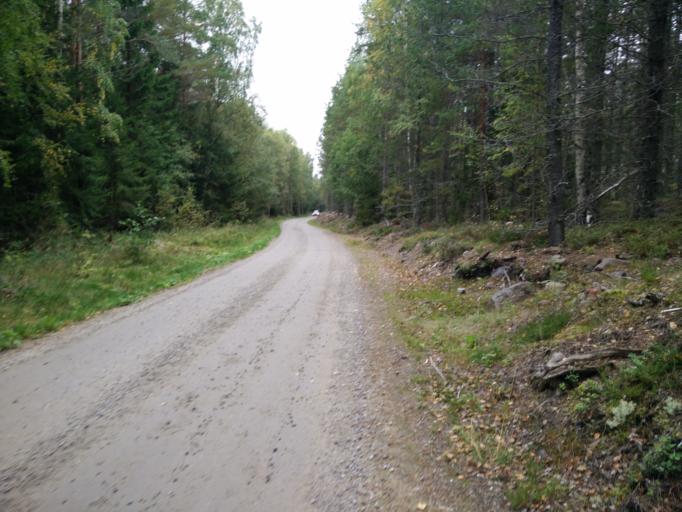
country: SE
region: Gaevleborg
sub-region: Hudiksvalls Kommun
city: Hudiksvall
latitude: 61.8331
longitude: 17.3332
